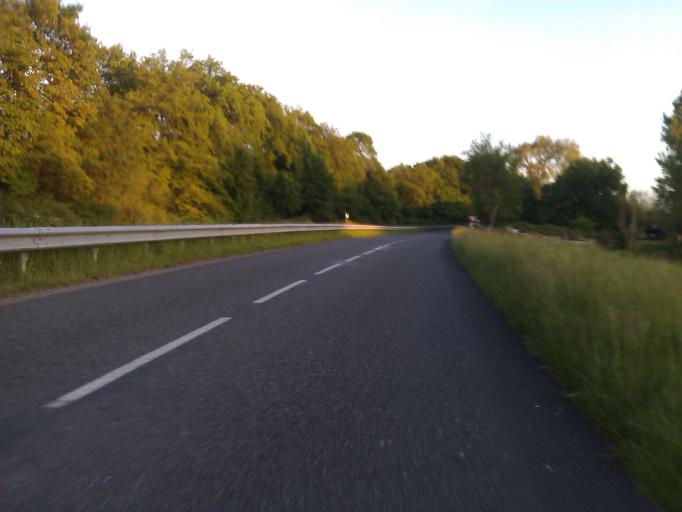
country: FR
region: Bourgogne
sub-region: Departement de Saone-et-Loire
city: Paray-le-Monial
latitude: 46.4542
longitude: 4.1581
